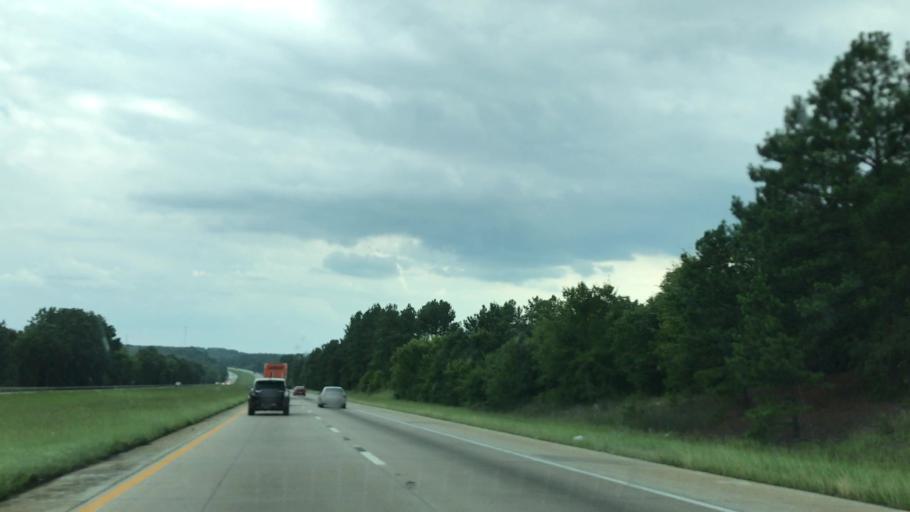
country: US
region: South Carolina
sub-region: Fairfield County
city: Winnsboro Mills
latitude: 34.3374
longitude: -81.0036
